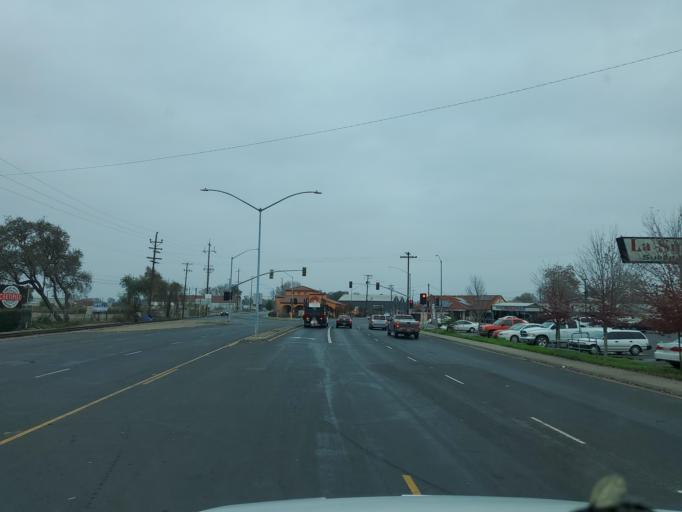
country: US
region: California
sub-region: San Joaquin County
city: August
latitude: 37.9725
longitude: -121.2683
